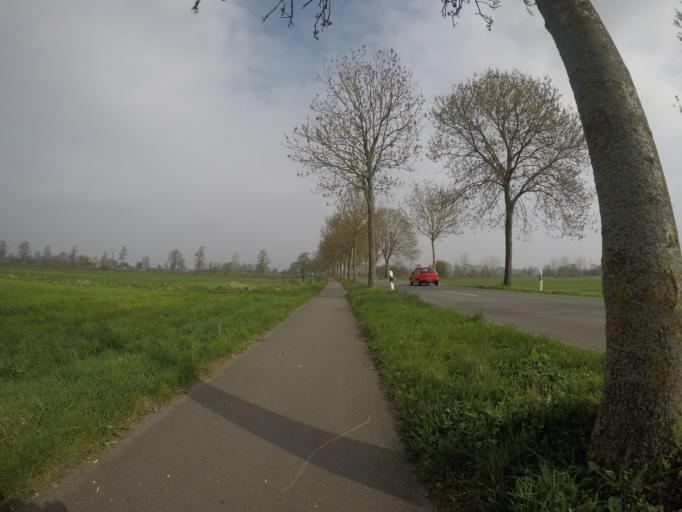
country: DE
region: North Rhine-Westphalia
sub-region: Regierungsbezirk Munster
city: Isselburg
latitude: 51.8497
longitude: 6.5040
